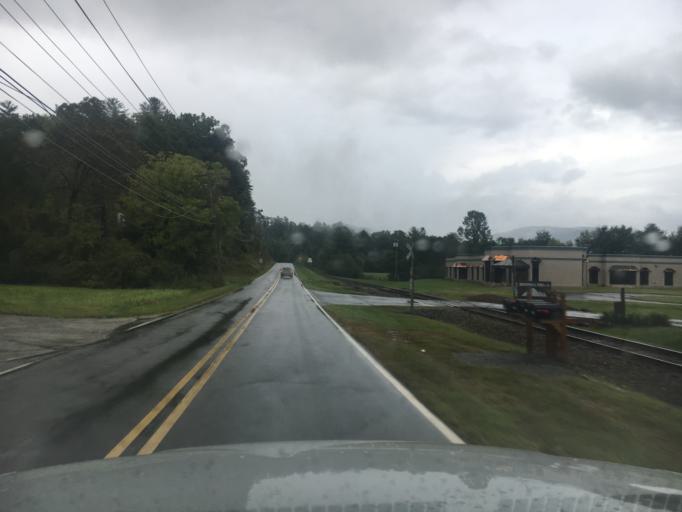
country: US
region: North Carolina
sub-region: Transylvania County
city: Brevard
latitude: 35.2599
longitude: -82.6787
